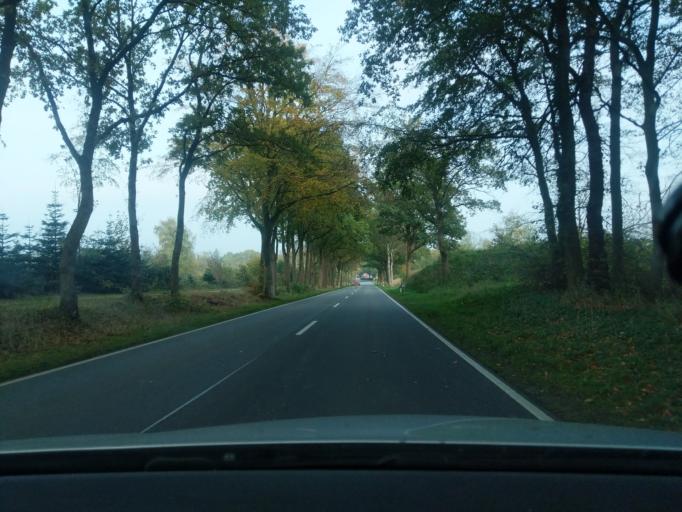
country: DE
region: Lower Saxony
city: Kranenburg
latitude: 53.6287
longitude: 9.2013
